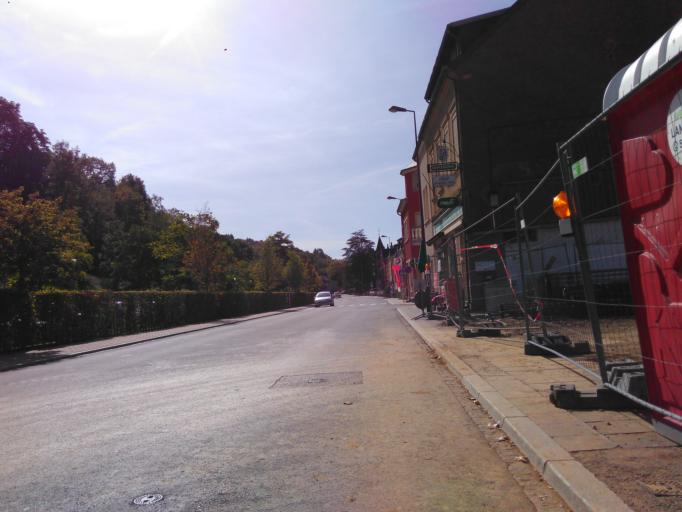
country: LU
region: Luxembourg
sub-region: Canton d'Esch-sur-Alzette
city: Rumelange
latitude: 49.4590
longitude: 6.0316
